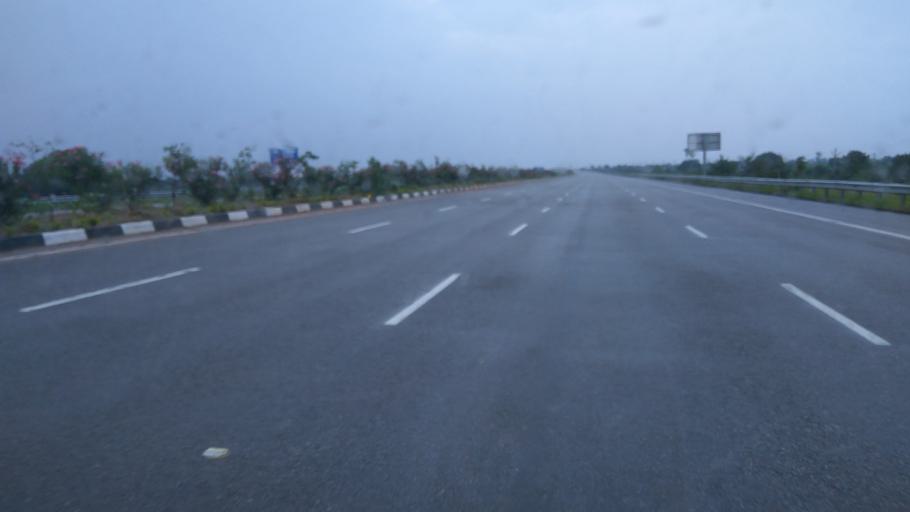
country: IN
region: Telangana
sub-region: Rangareddi
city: Ghatkesar
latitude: 17.4818
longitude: 78.6673
